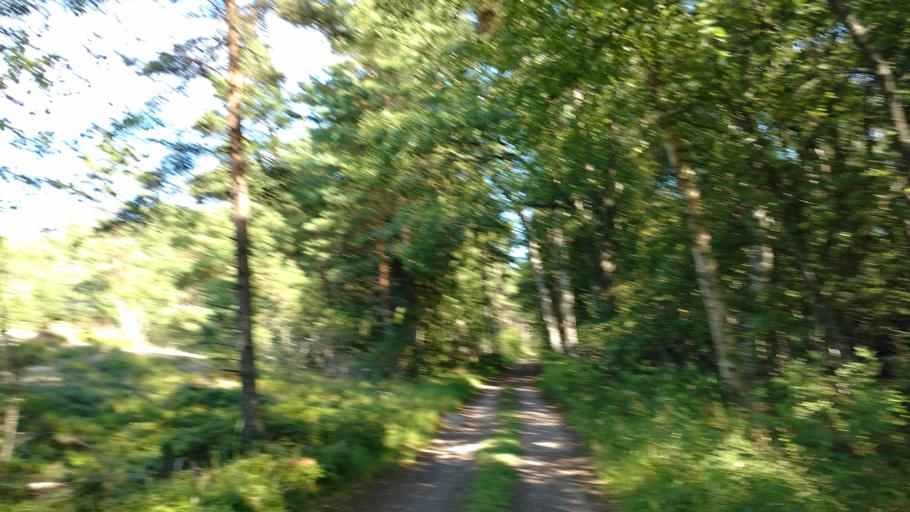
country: FI
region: Varsinais-Suomi
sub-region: Aboland-Turunmaa
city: Dragsfjaerd
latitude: 59.8079
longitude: 22.3297
